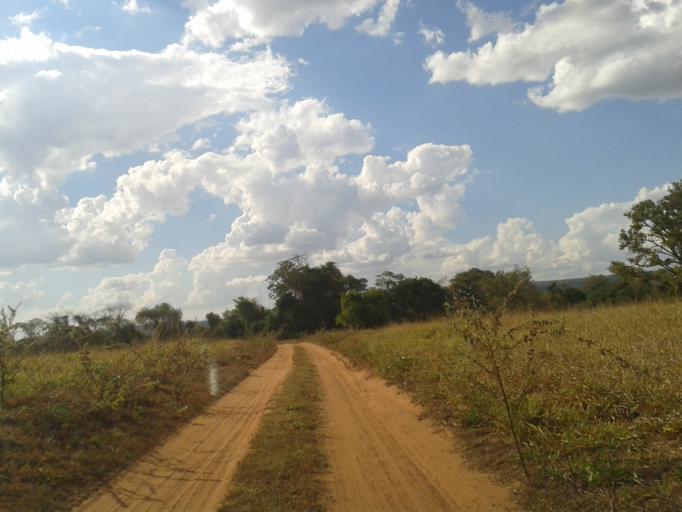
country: BR
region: Minas Gerais
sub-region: Santa Vitoria
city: Santa Vitoria
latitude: -19.1677
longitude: -50.0217
